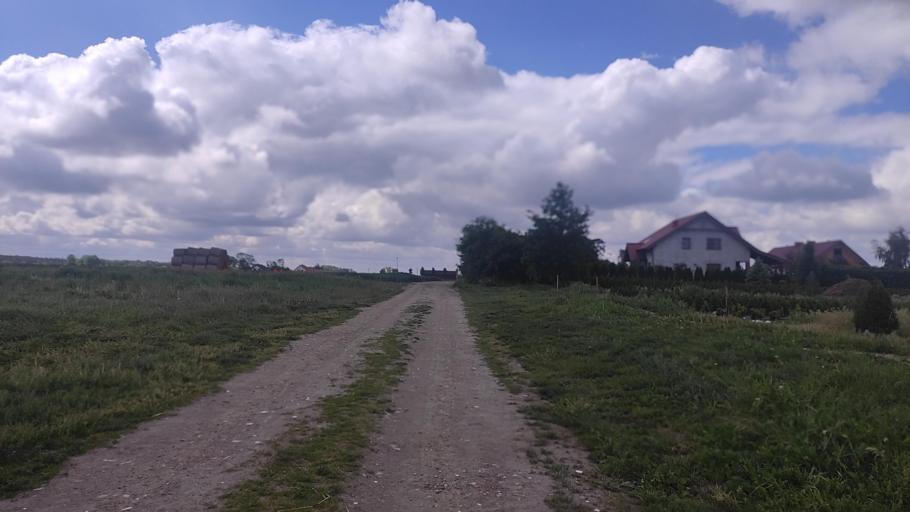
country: PL
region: Greater Poland Voivodeship
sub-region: Powiat poznanski
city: Kostrzyn
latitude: 52.4172
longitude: 17.1739
